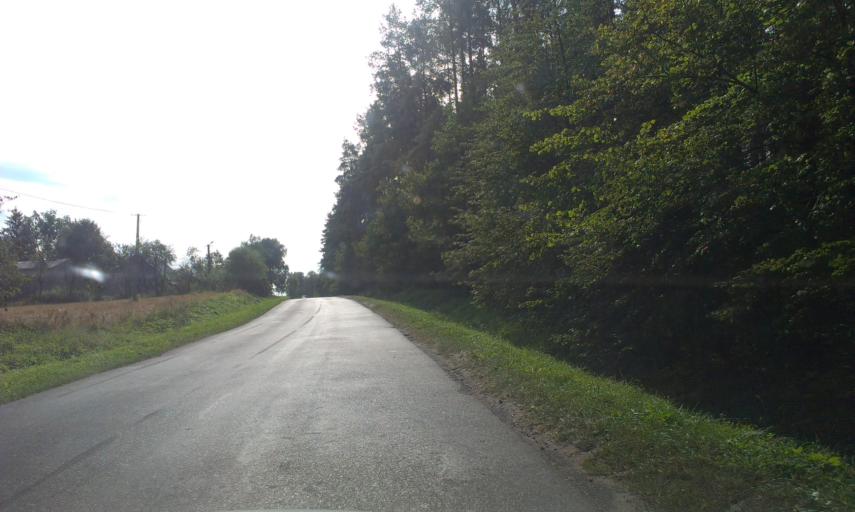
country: PL
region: Greater Poland Voivodeship
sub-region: Powiat zlotowski
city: Zlotow
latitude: 53.4369
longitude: 16.9841
